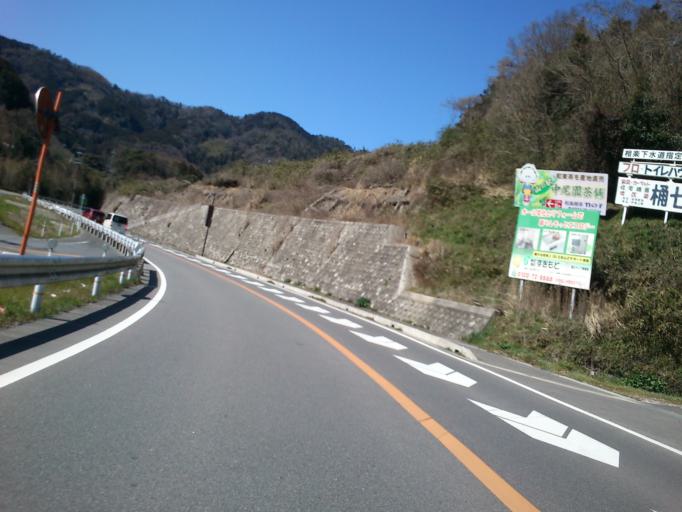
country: JP
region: Nara
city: Nara-shi
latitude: 34.7762
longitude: 135.8811
